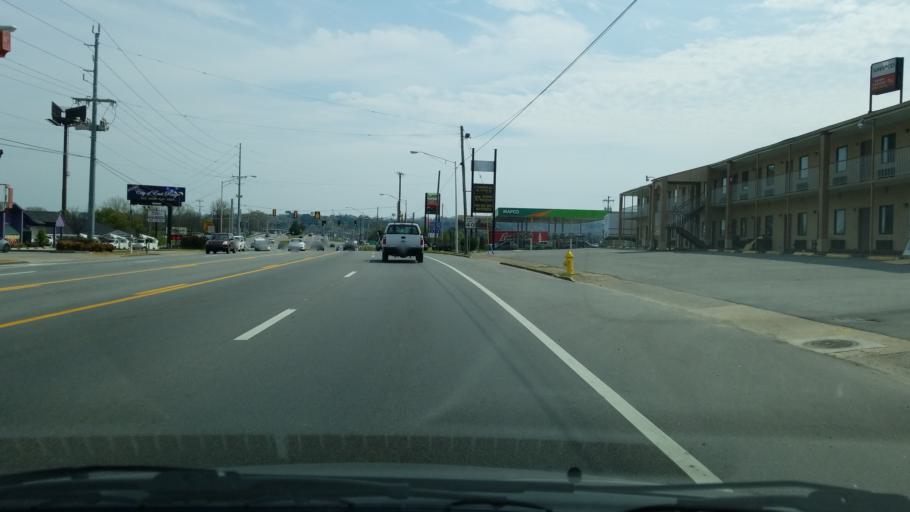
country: US
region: Tennessee
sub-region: Hamilton County
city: East Ridge
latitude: 34.9894
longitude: -85.2085
